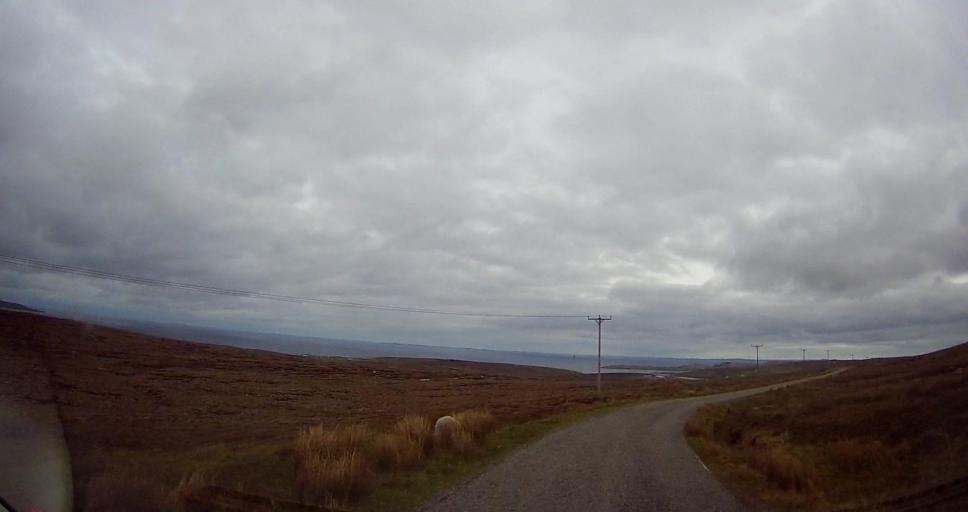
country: GB
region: Scotland
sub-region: Shetland Islands
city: Shetland
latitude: 60.5737
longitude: -1.0673
